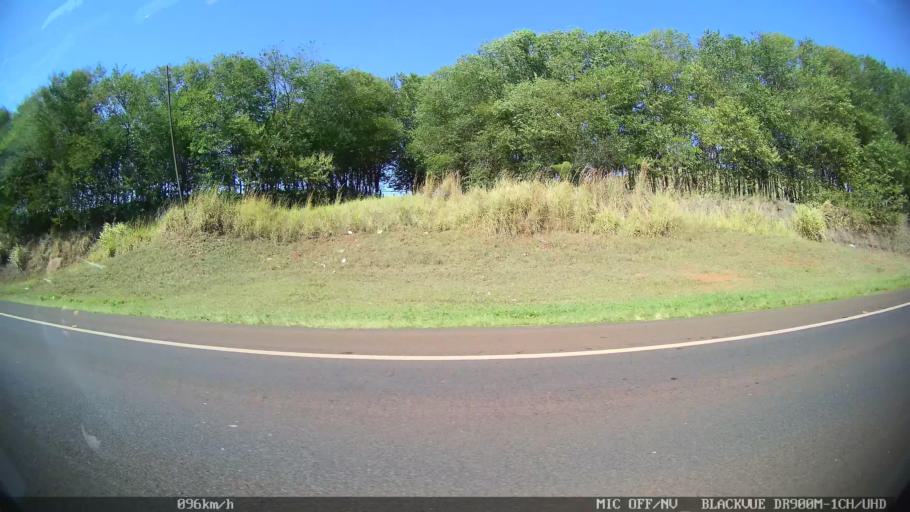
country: BR
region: Sao Paulo
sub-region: Franca
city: Franca
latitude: -20.5845
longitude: -47.4321
